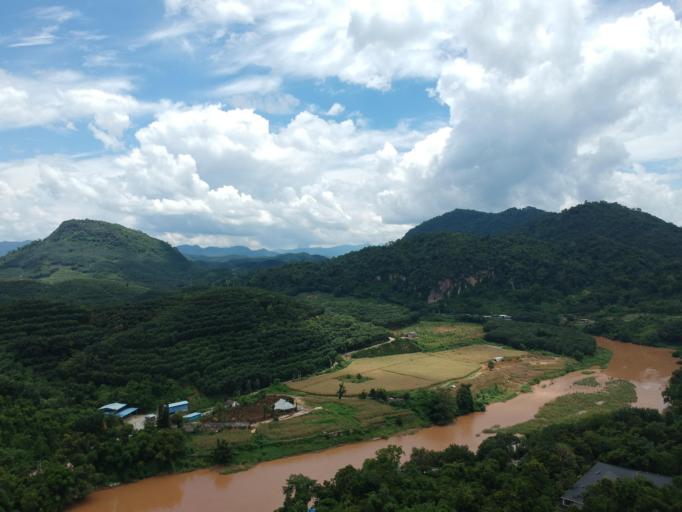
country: CN
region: Yunnan
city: Mengla
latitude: 21.9217
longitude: 101.2753
